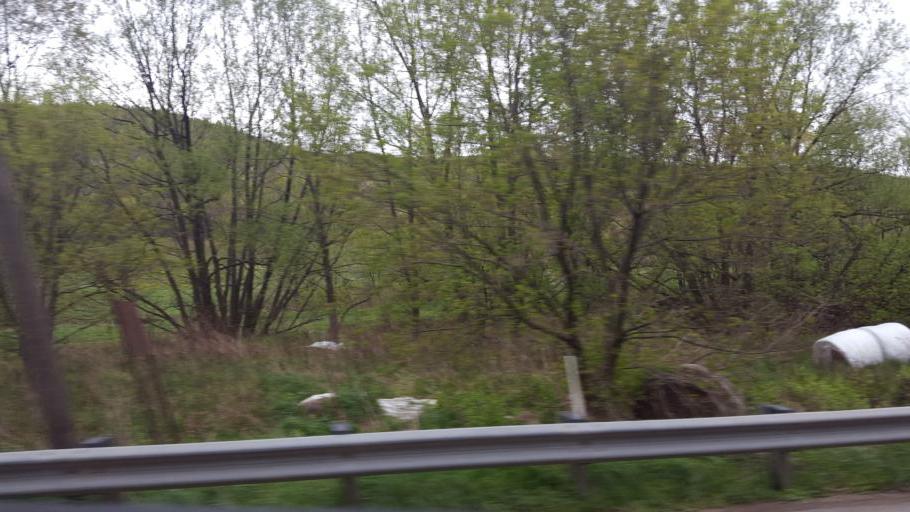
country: US
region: Pennsylvania
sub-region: Tioga County
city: Westfield
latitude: 41.9429
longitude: -77.6645
